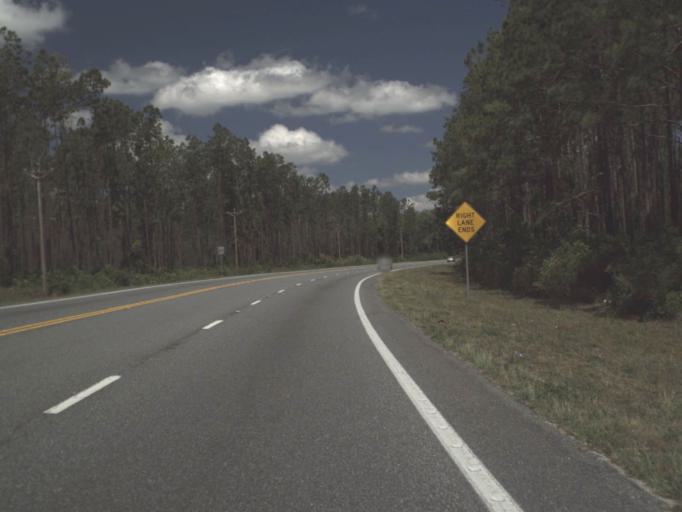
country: US
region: Florida
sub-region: Marion County
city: Silver Springs Shores
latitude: 29.1867
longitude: -81.9031
